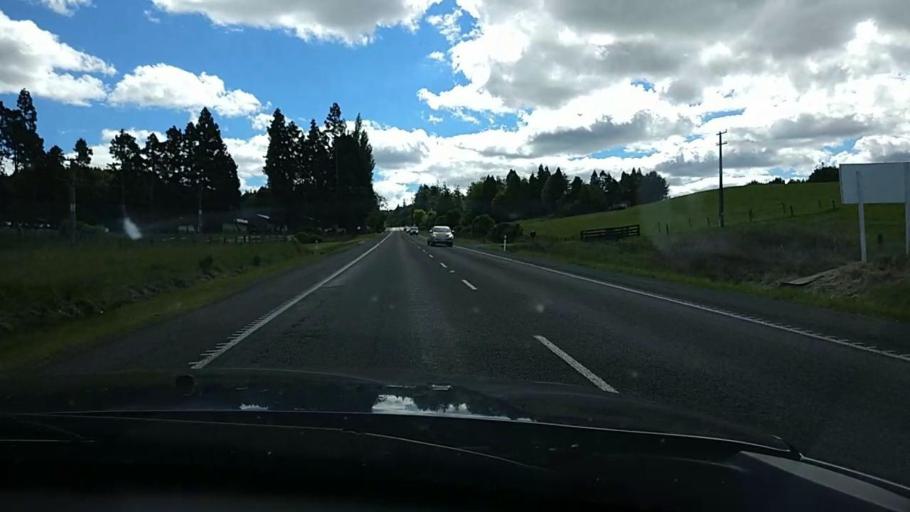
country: NZ
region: Bay of Plenty
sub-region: Rotorua District
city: Rotorua
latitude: -38.0708
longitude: 176.1380
